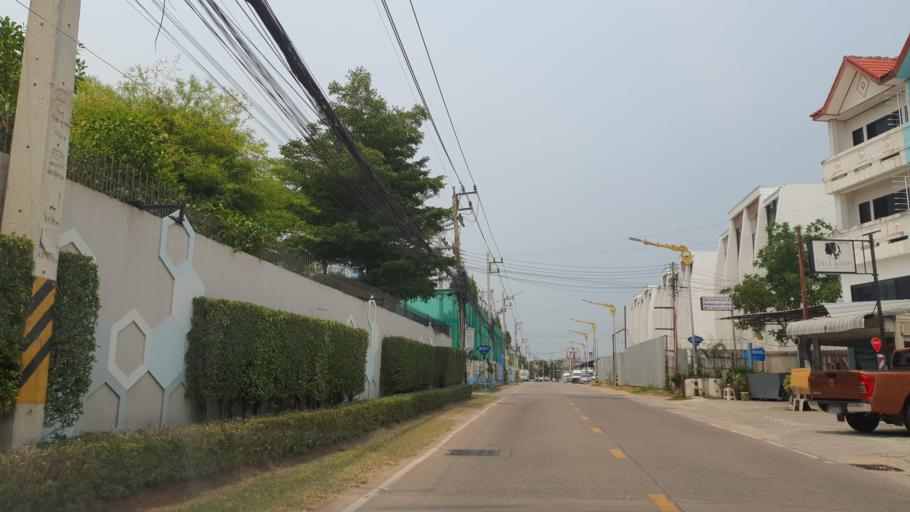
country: TH
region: Chon Buri
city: Phatthaya
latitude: 12.8958
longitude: 100.9083
